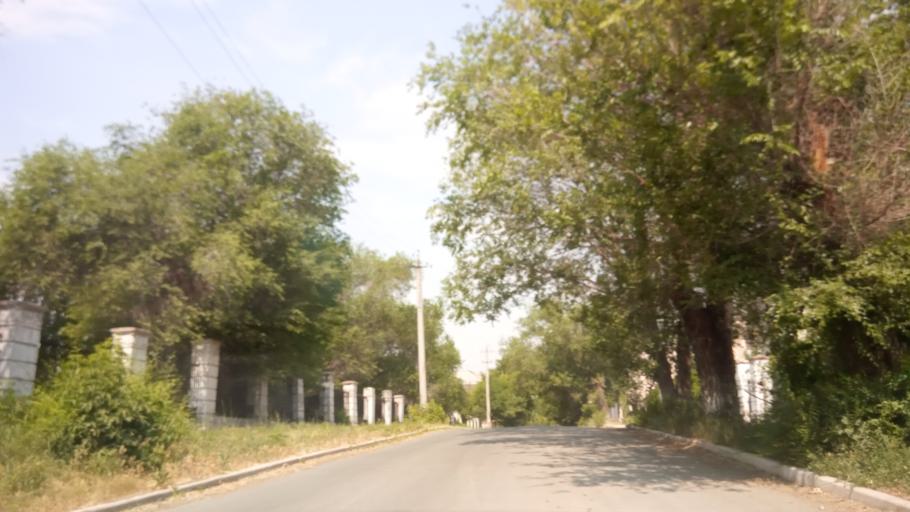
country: RU
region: Orenburg
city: Novotroitsk
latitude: 51.1956
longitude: 58.3321
